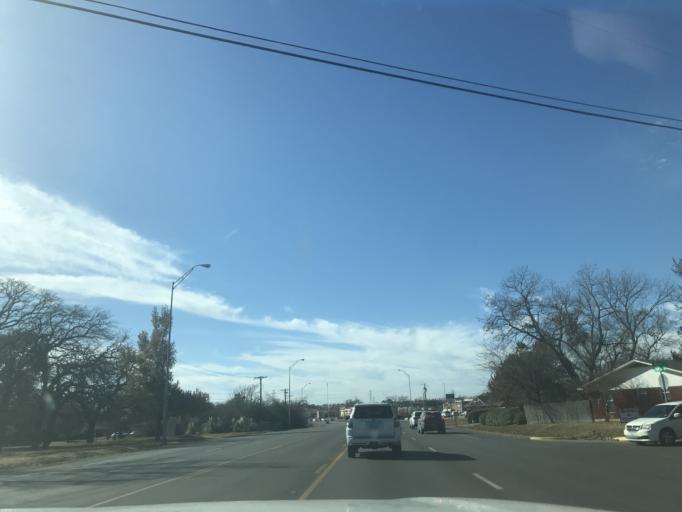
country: US
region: Texas
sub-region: Erath County
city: Stephenville
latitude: 32.2075
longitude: -98.2268
